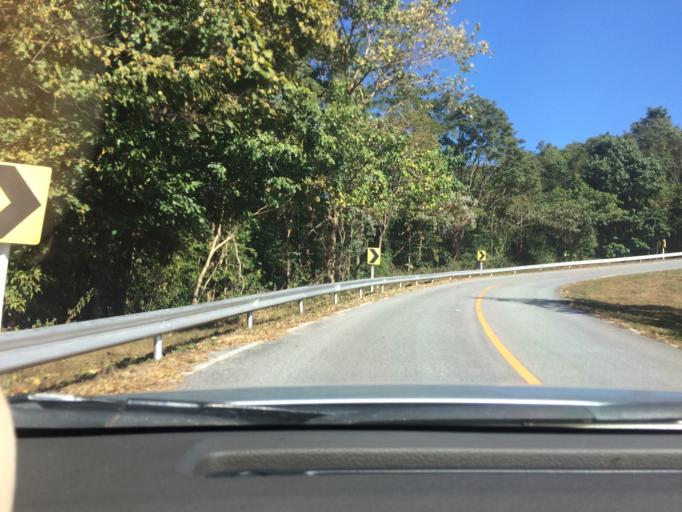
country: TH
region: Phitsanulok
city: Nakhon Thai
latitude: 17.0216
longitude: 100.9636
